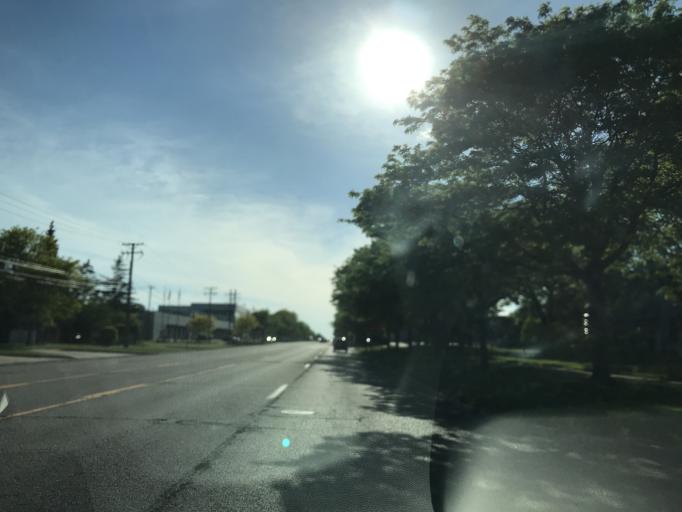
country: US
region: Michigan
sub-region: Oakland County
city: Farmington
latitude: 42.4410
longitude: -83.3616
